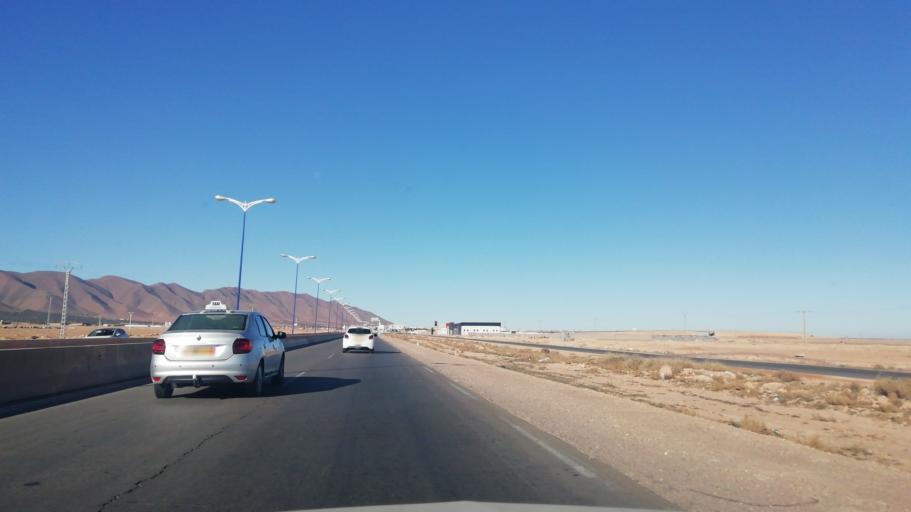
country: DZ
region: Wilaya de Naama
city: Naama
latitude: 33.5042
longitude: -0.2876
